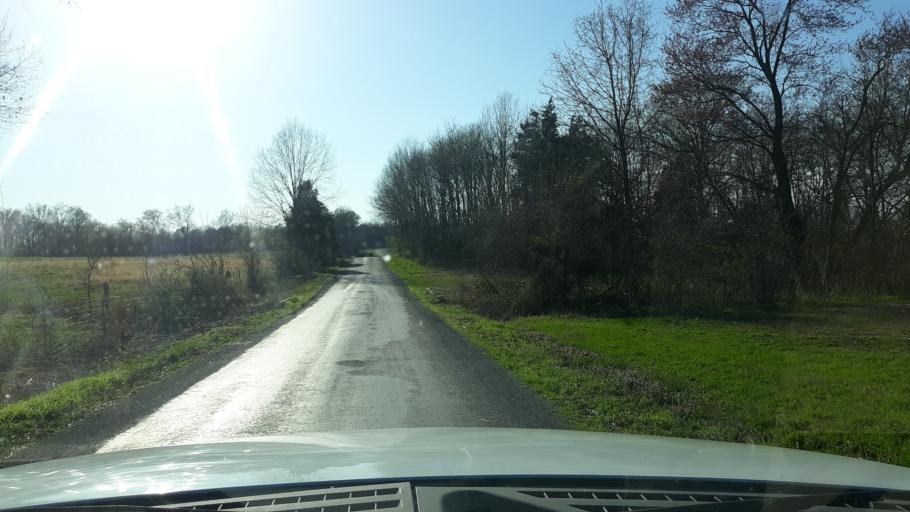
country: US
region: Illinois
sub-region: Saline County
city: Harrisburg
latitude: 37.7846
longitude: -88.6020
